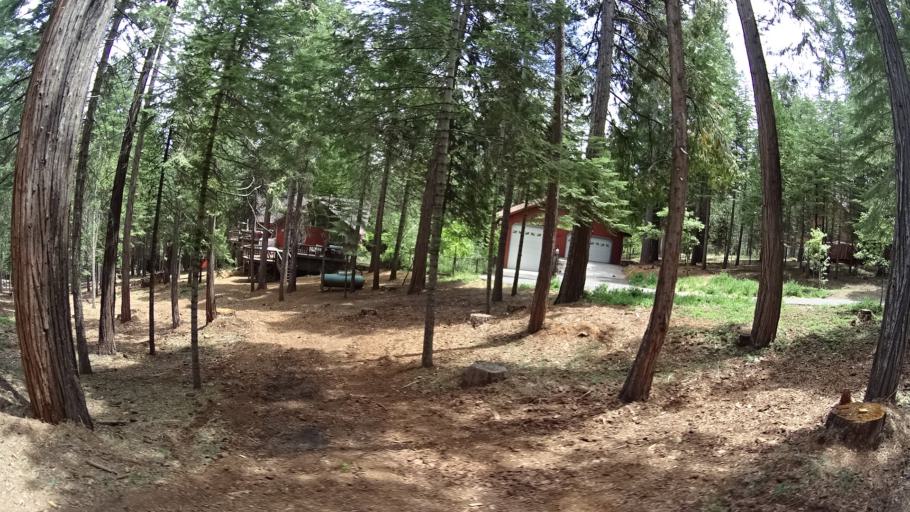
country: US
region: California
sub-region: Calaveras County
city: Arnold
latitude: 38.2378
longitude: -120.3461
